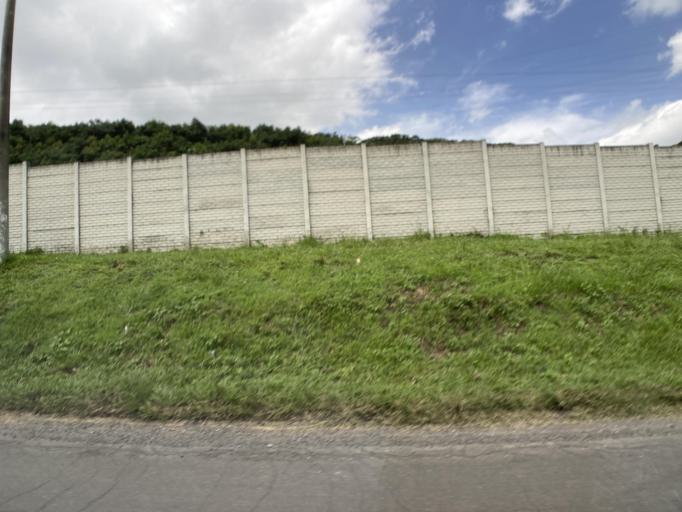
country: GT
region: Guatemala
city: Amatitlan
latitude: 14.4641
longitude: -90.5889
